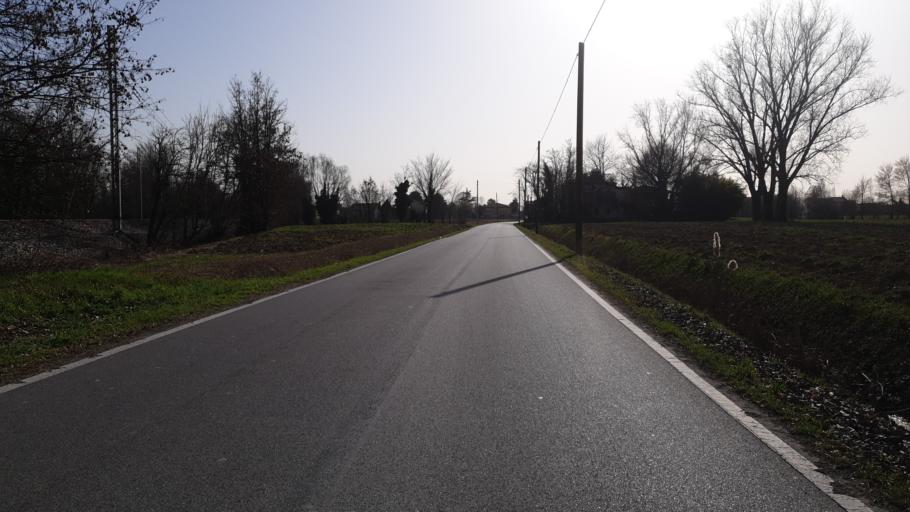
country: IT
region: Veneto
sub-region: Provincia di Padova
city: Vigodarzere
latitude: 45.4713
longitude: 11.8926
